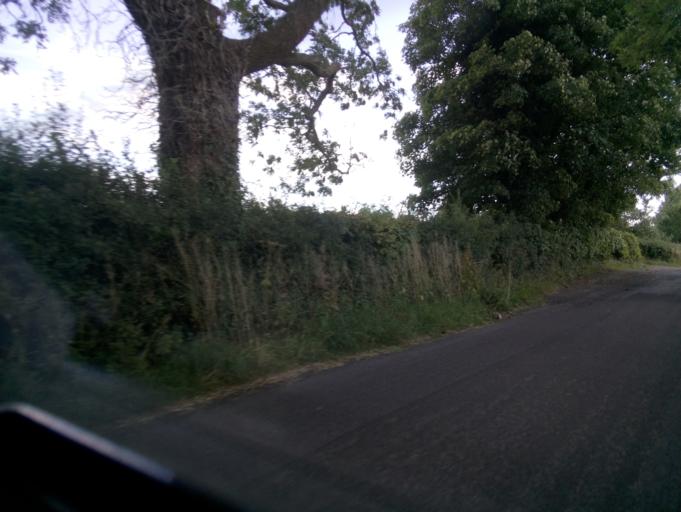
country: GB
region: England
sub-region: Gloucestershire
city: Tetbury
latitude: 51.6522
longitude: -2.1441
